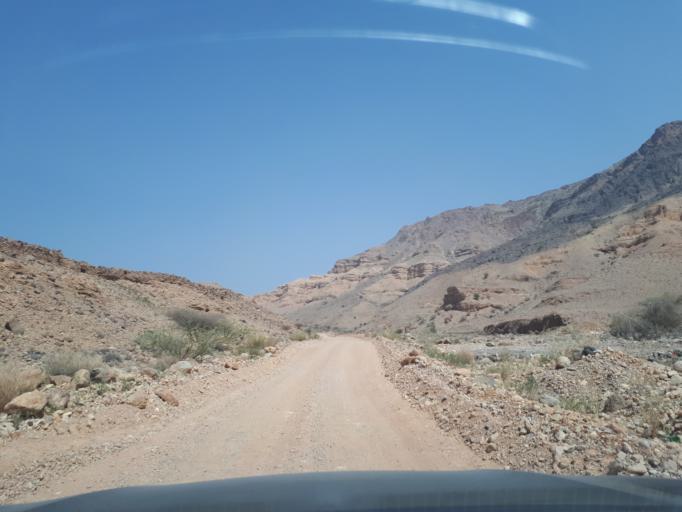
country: OM
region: Ash Sharqiyah
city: Ibra'
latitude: 23.0760
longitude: 58.8765
